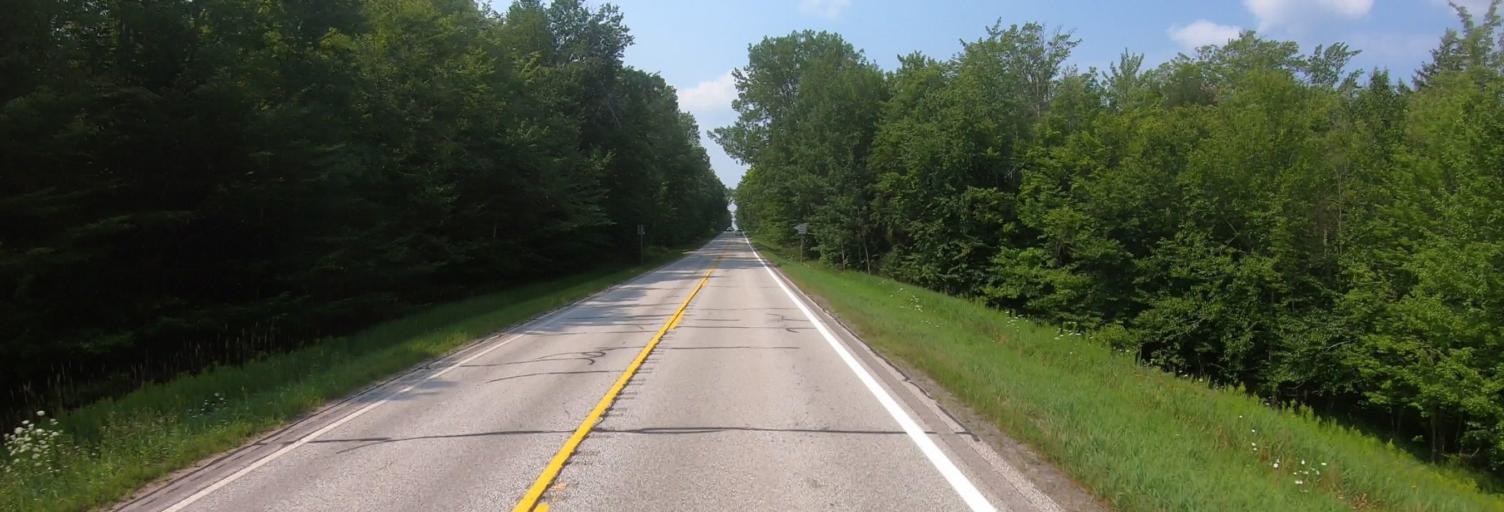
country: US
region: Michigan
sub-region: Luce County
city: Newberry
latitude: 46.5280
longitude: -85.4049
